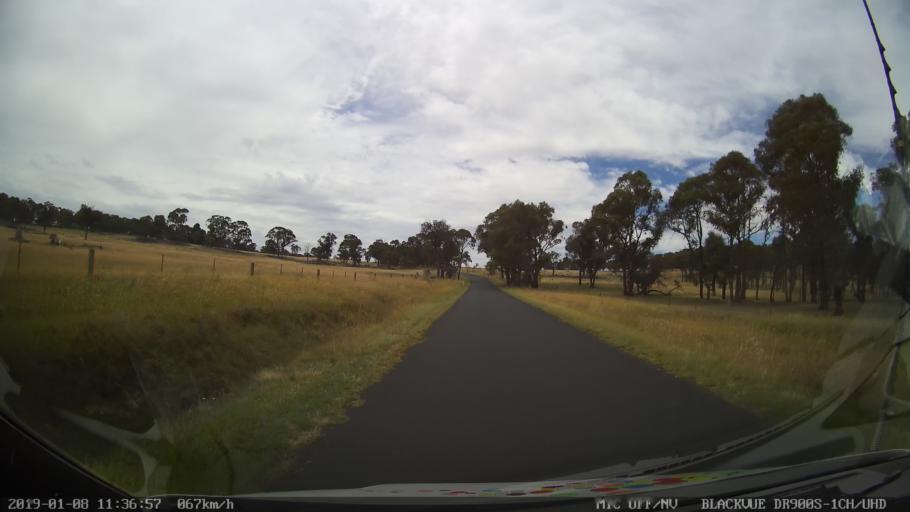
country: AU
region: New South Wales
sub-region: Guyra
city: Guyra
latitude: -30.3489
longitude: 151.5480
